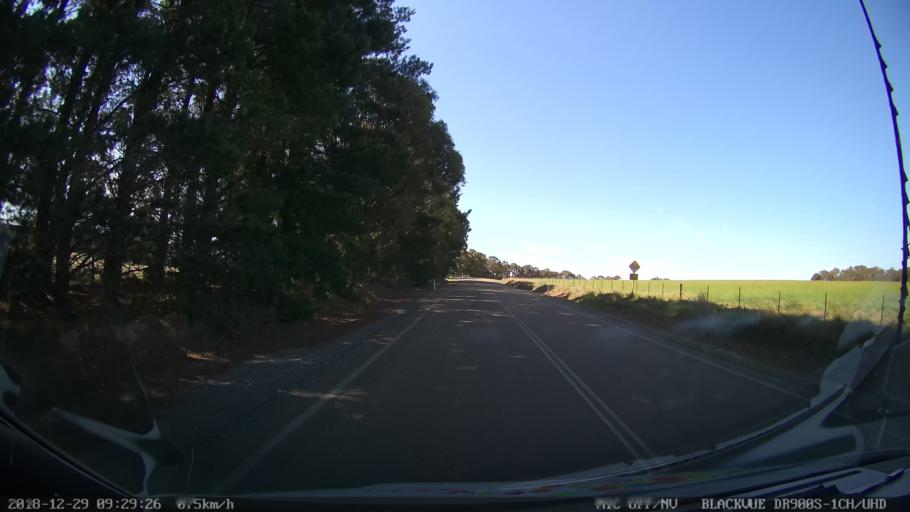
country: AU
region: New South Wales
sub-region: Upper Lachlan Shire
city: Crookwell
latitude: -34.5884
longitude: 149.3745
